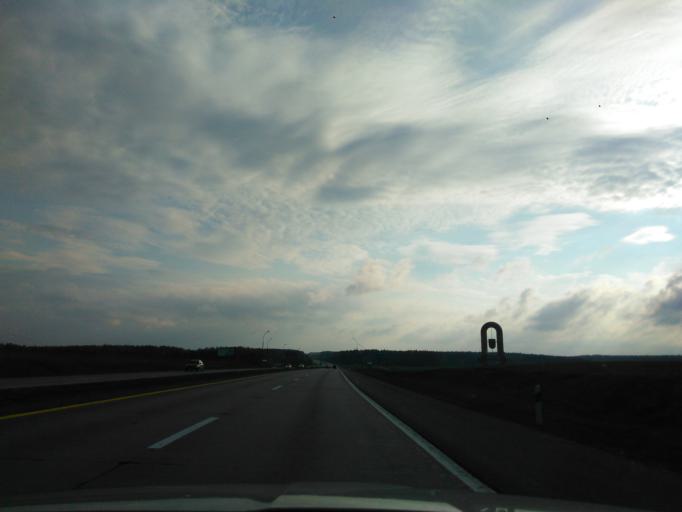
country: BY
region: Minsk
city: Astrashytski Haradok
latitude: 54.0965
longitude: 27.7836
